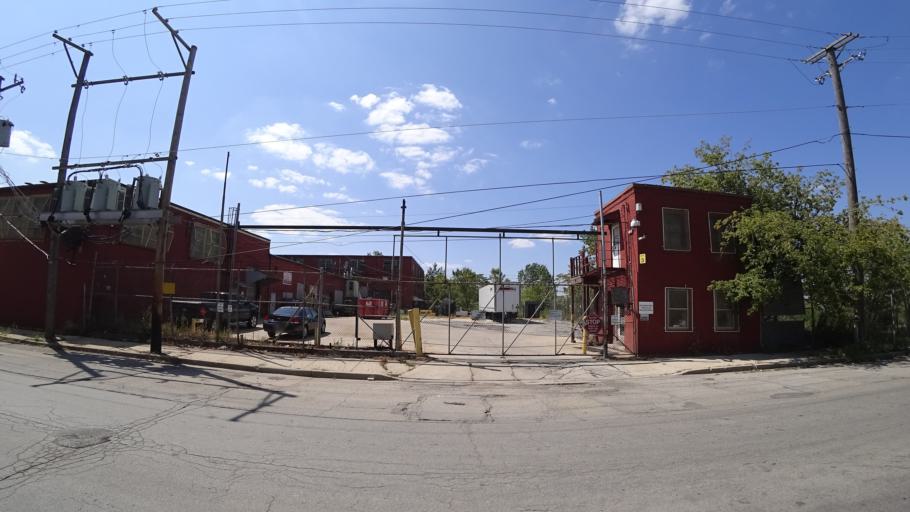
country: US
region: Illinois
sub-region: Cook County
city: Cicero
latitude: 41.8620
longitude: -87.7372
